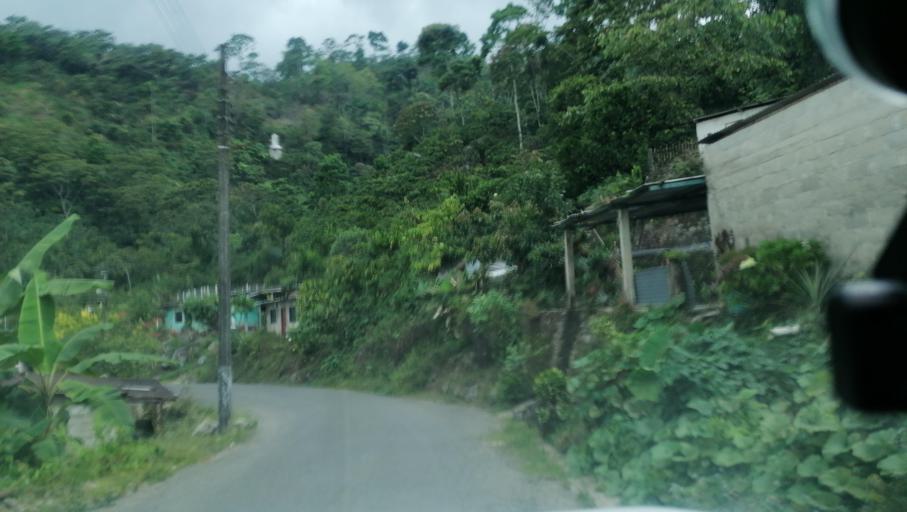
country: MX
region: Chiapas
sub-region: Cacahoatan
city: Benito Juarez
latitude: 15.0760
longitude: -92.1727
